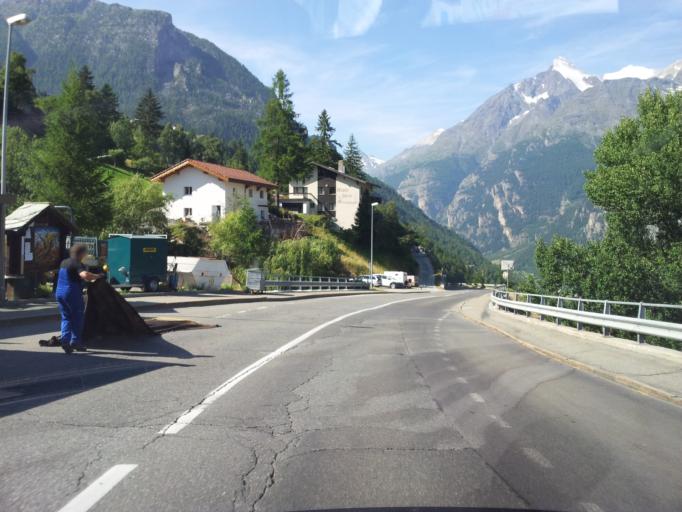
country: CH
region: Valais
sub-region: Visp District
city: Grachen
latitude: 46.1881
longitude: 7.8224
